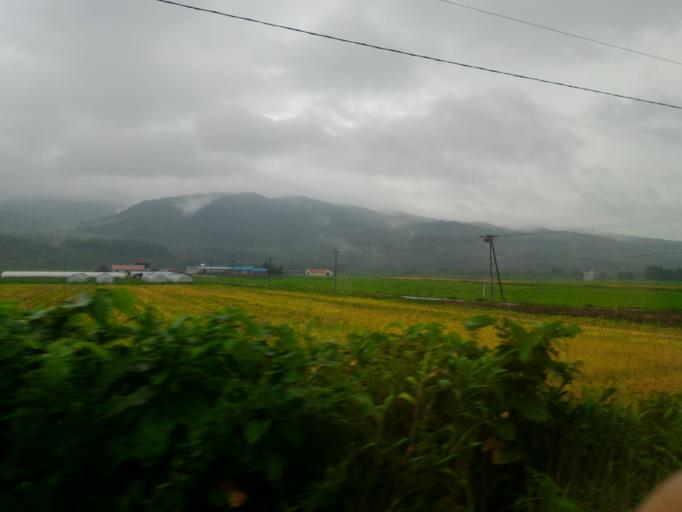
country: JP
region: Hokkaido
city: Nayoro
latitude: 44.5663
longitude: 142.3160
